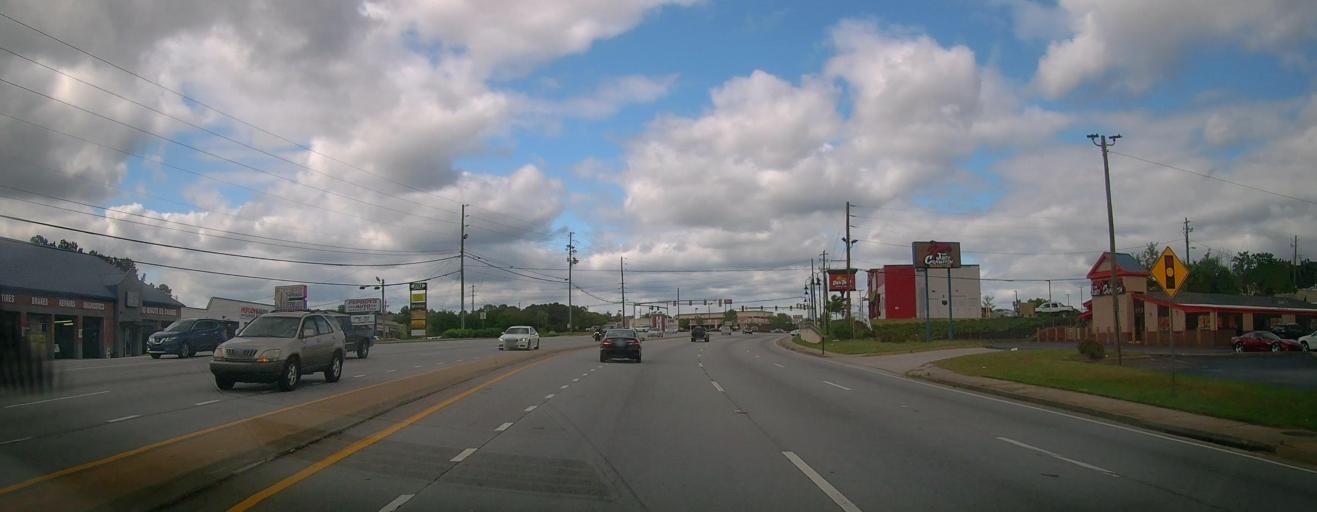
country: US
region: Georgia
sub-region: Rockdale County
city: Conyers
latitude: 33.6438
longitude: -84.0145
